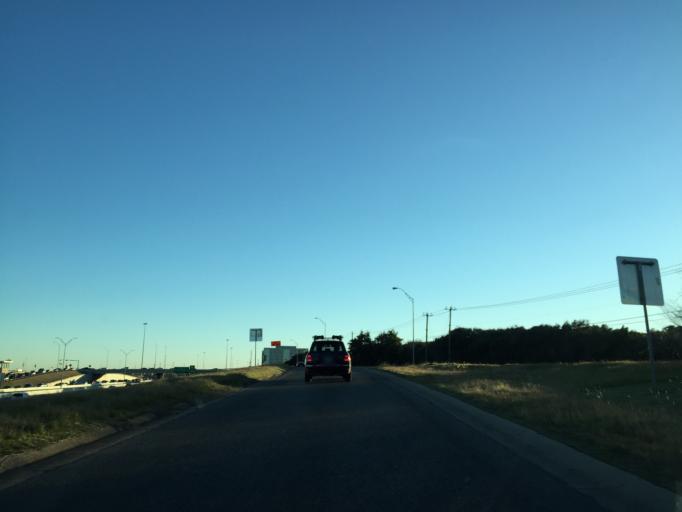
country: US
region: Texas
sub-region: Williamson County
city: Jollyville
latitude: 30.3935
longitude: -97.7339
